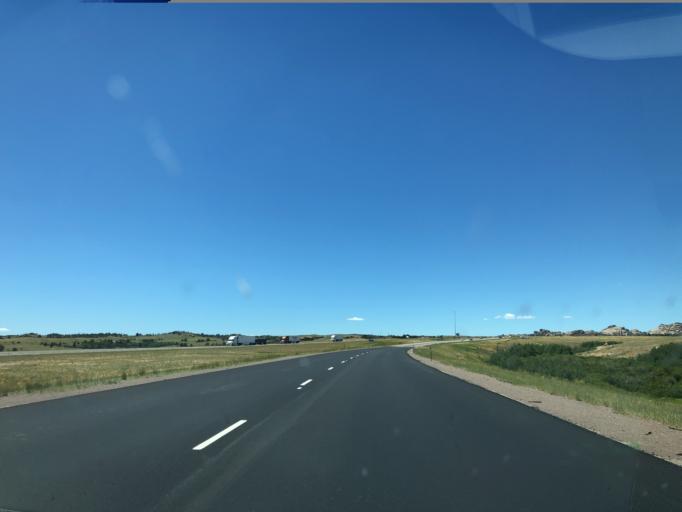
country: US
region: Wyoming
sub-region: Albany County
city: Laramie
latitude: 41.1291
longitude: -105.3383
